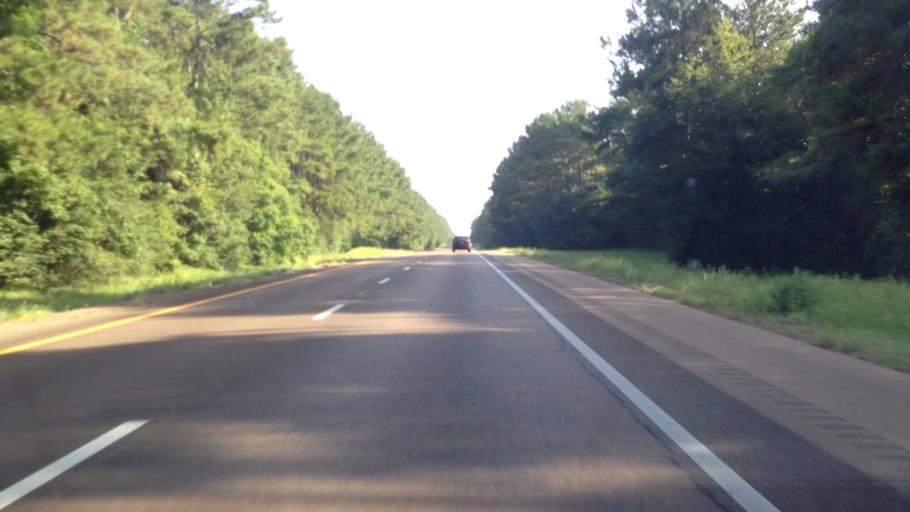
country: US
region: Mississippi
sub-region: Pike County
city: Summit
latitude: 31.3356
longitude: -90.4773
